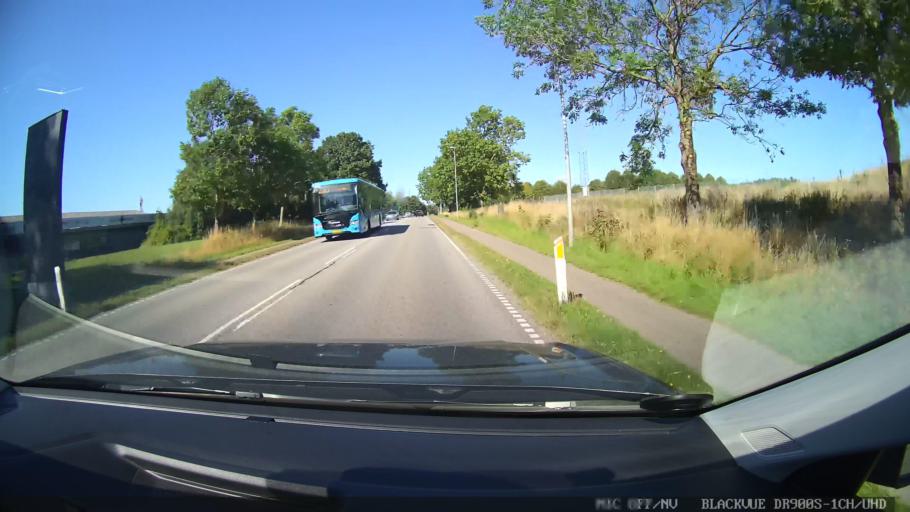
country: DK
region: Central Jutland
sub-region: Randers Kommune
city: Randers
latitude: 56.4933
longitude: 10.0249
